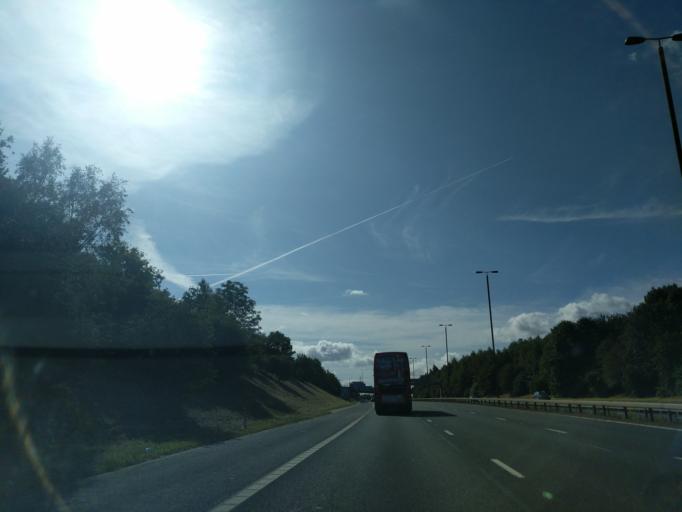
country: GB
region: England
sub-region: City and Borough of Leeds
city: Lofthouse
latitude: 53.7606
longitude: -1.5136
